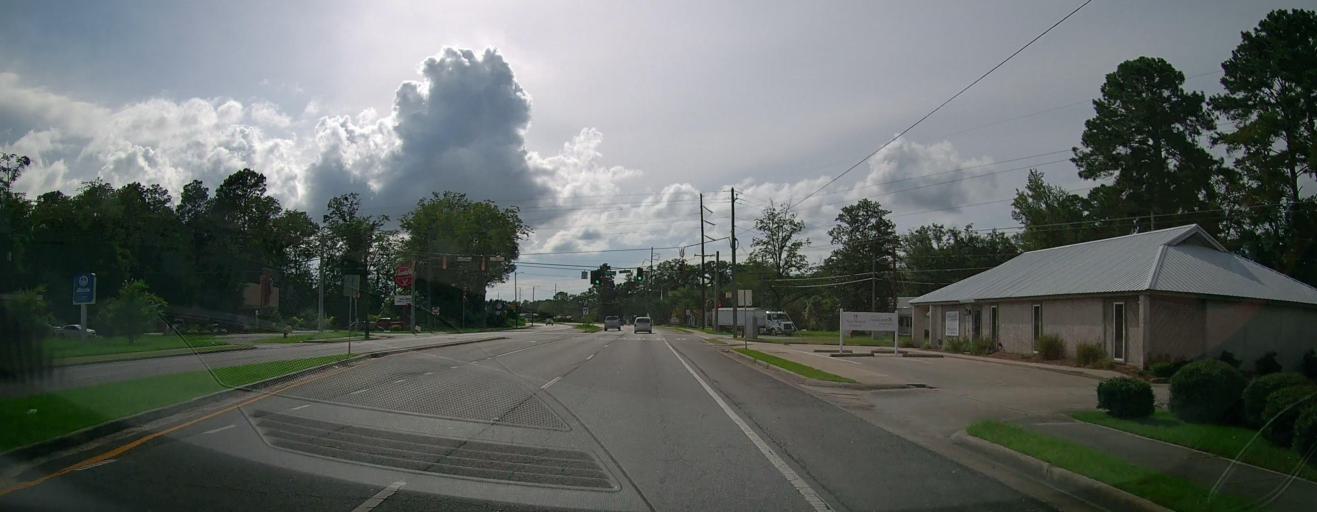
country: US
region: Georgia
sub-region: Wayne County
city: Jesup
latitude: 31.6034
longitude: -81.8998
